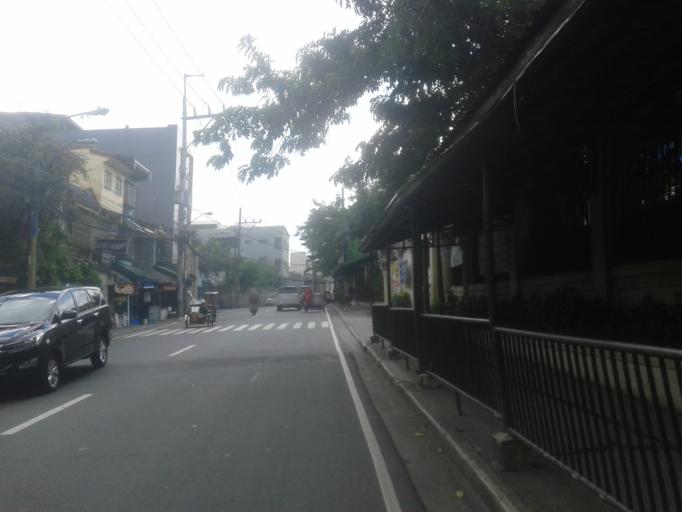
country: PH
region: Metro Manila
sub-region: Mandaluyong
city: Mandaluyong City
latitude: 14.5837
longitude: 121.0448
